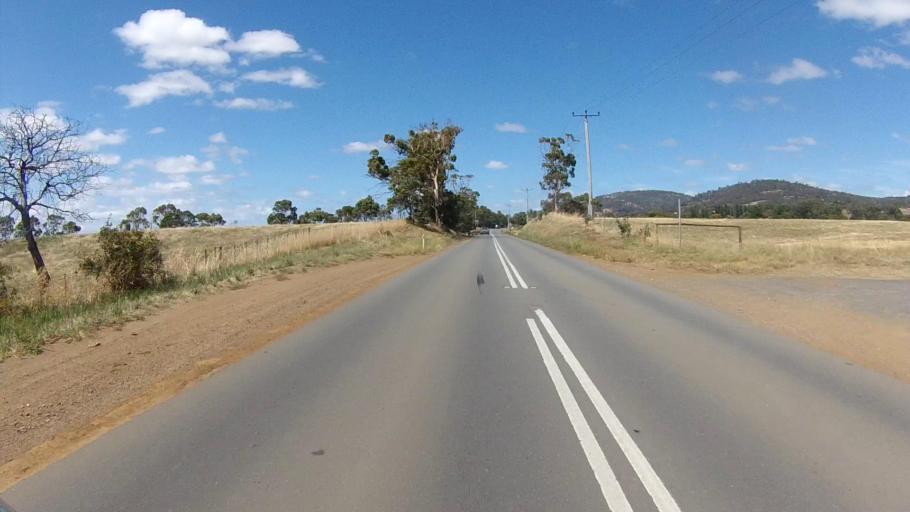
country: AU
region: Tasmania
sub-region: Clarence
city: Cambridge
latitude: -42.7673
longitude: 147.4159
